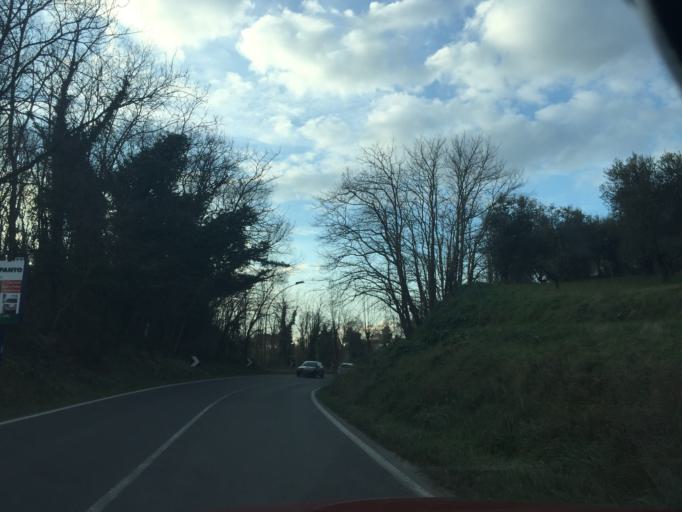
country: IT
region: Tuscany
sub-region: Provincia di Pistoia
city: Lamporecchio
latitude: 43.8188
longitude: 10.8841
